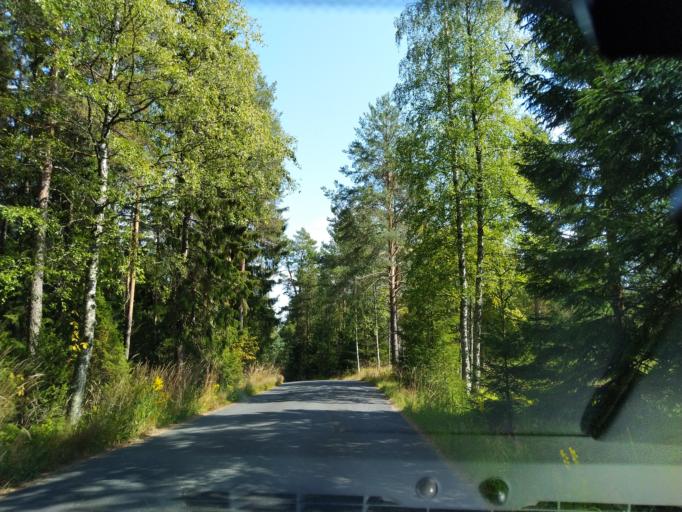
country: FI
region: Uusimaa
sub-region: Helsinki
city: Karkkila
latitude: 60.7182
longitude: 24.1863
